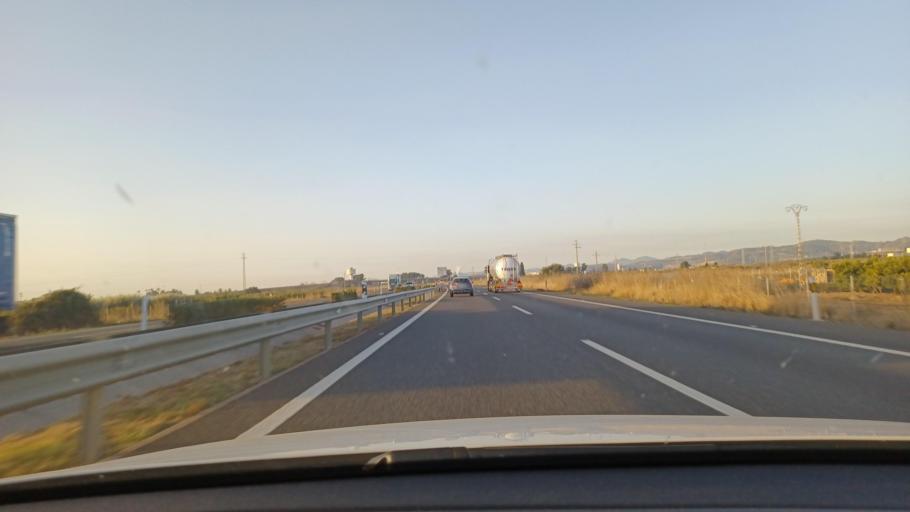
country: ES
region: Valencia
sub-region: Provincia de Castello
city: Moncofar
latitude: 39.8176
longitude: -0.1516
